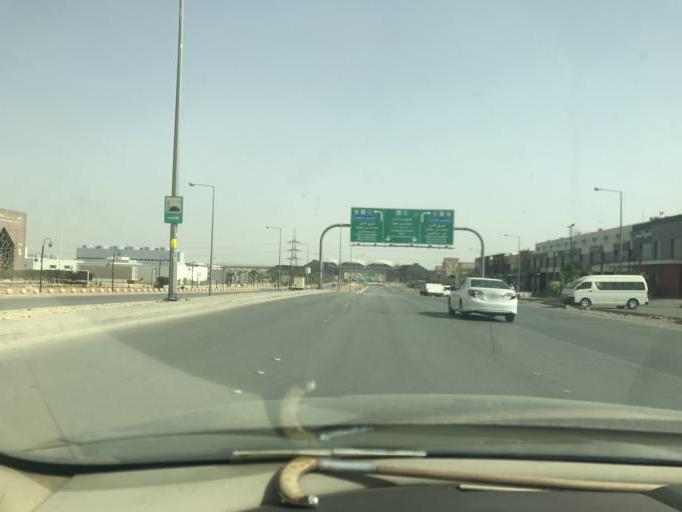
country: SA
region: Ar Riyad
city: Riyadh
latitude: 24.8065
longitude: 46.6934
